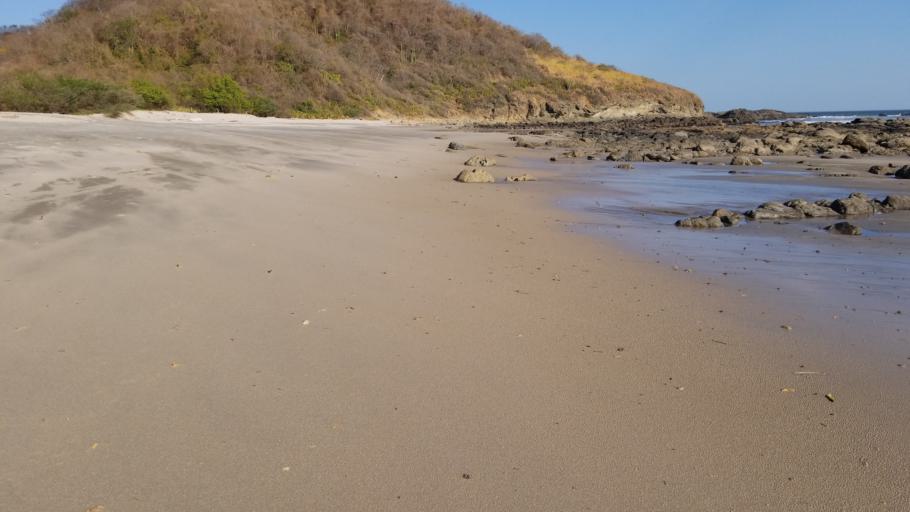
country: NI
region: Rivas
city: Tola
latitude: 11.4800
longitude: -86.1491
